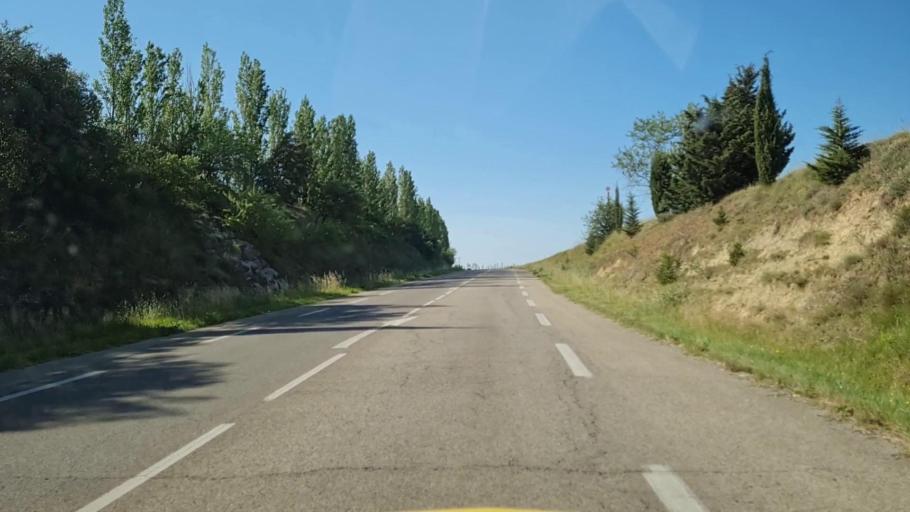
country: FR
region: Languedoc-Roussillon
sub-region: Departement du Gard
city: Garons
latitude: 43.7328
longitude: 4.4105
